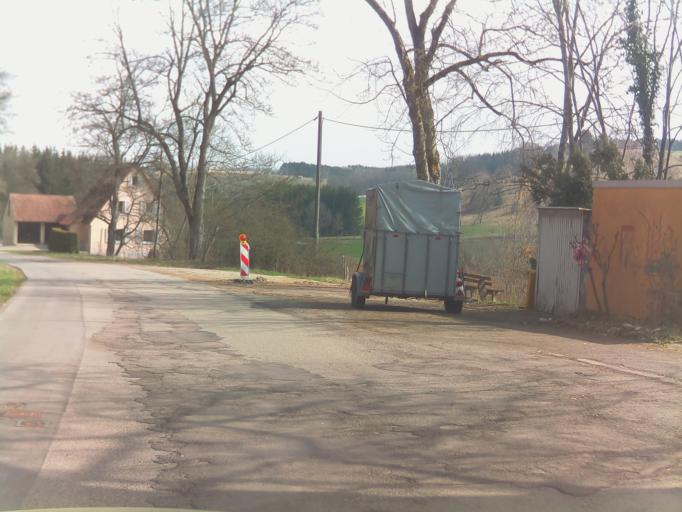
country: DE
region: Baden-Wuerttemberg
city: Altes Lager
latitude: 48.4162
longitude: 9.5408
